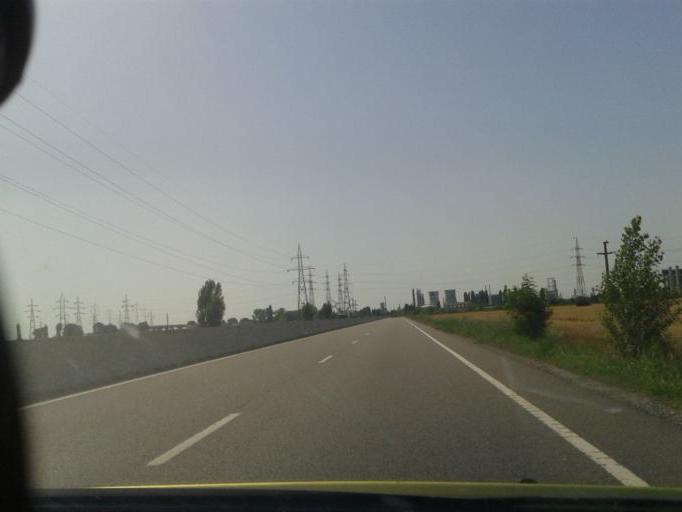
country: RO
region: Prahova
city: Brazii de Sus
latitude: 44.8910
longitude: 26.0093
